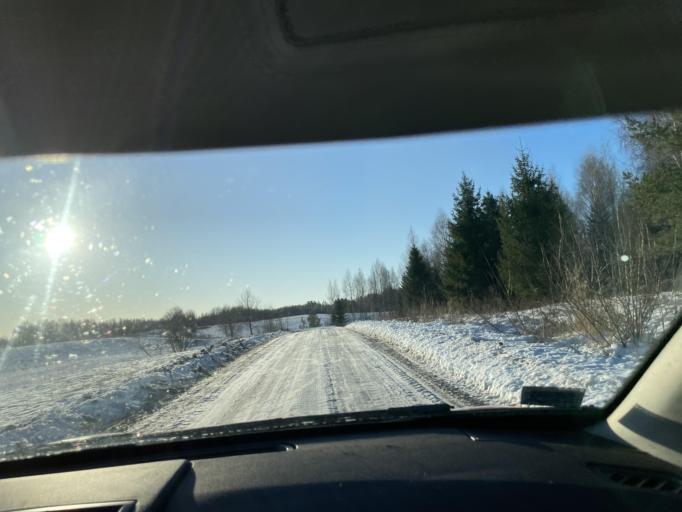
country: LV
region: Ludzas Rajons
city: Ludza
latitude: 56.4583
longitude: 27.6357
